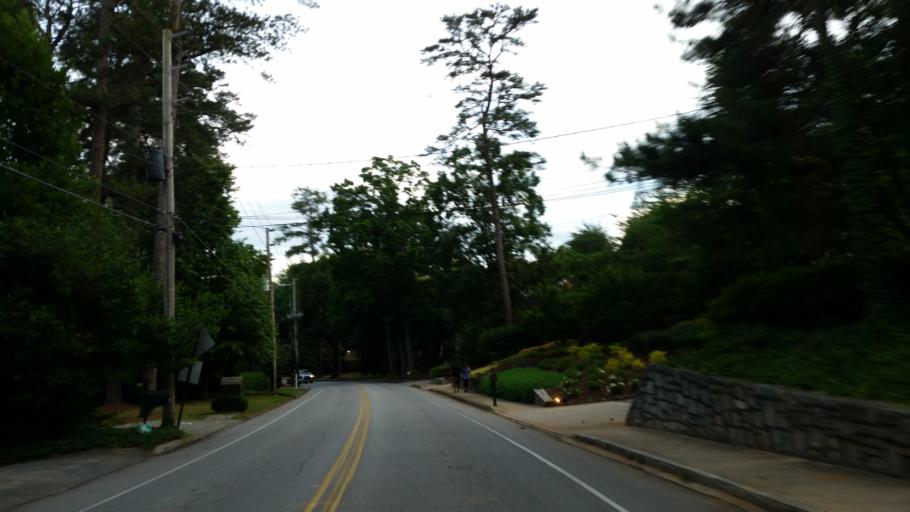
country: US
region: Georgia
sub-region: DeKalb County
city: North Atlanta
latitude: 33.8460
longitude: -84.3955
